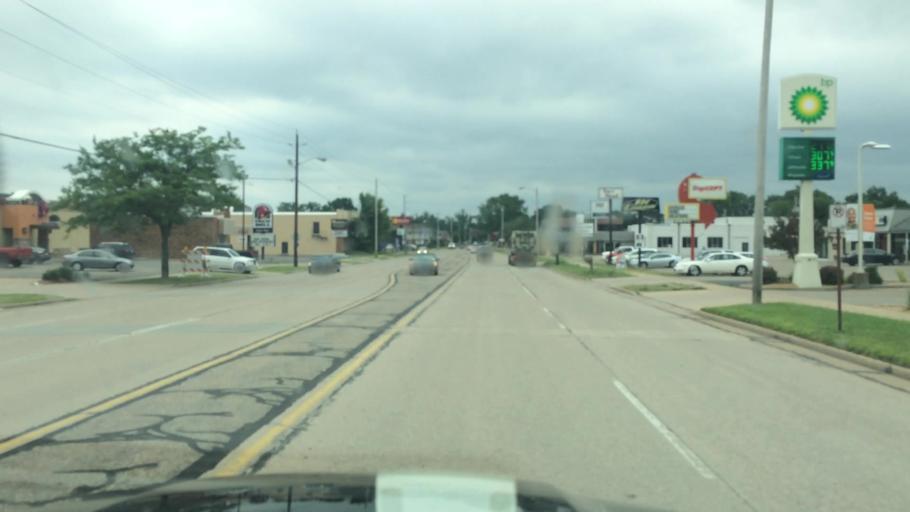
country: US
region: Wisconsin
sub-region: Portage County
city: Stevens Point
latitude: 44.5314
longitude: -89.5750
